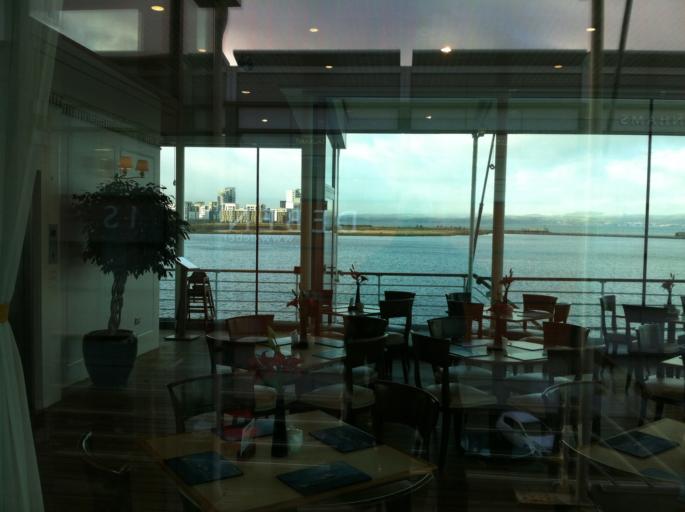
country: GB
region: Scotland
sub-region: West Lothian
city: Seafield
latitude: 55.9823
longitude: -3.1768
